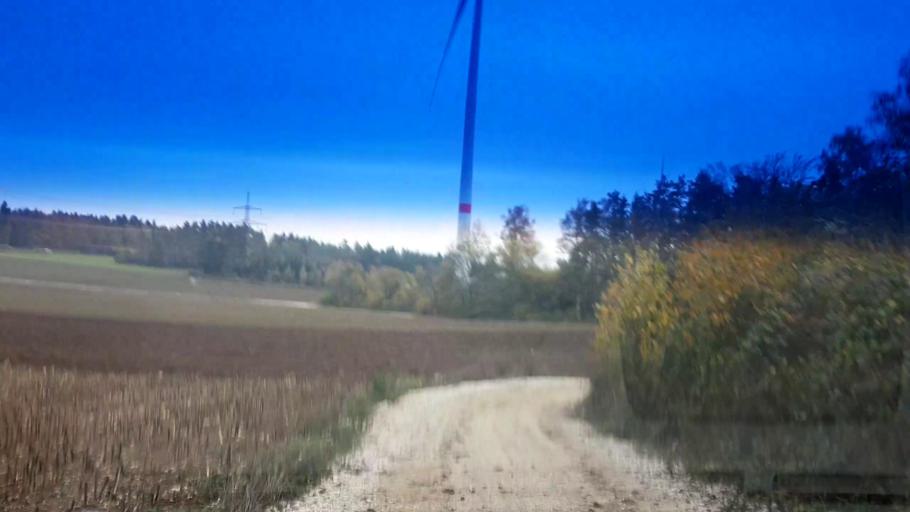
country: DE
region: Bavaria
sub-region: Upper Franconia
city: Poxdorf
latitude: 49.9340
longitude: 11.1019
